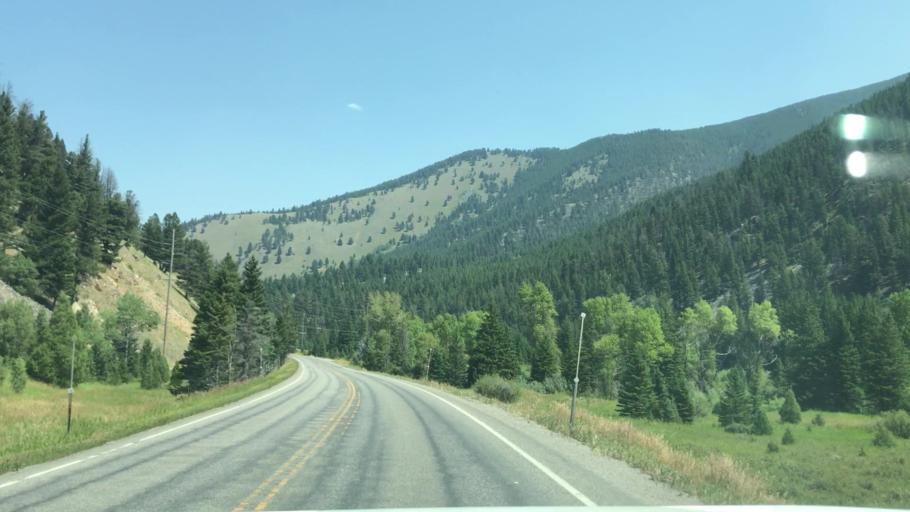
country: US
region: Montana
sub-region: Gallatin County
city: Big Sky
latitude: 45.2779
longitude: -111.2317
